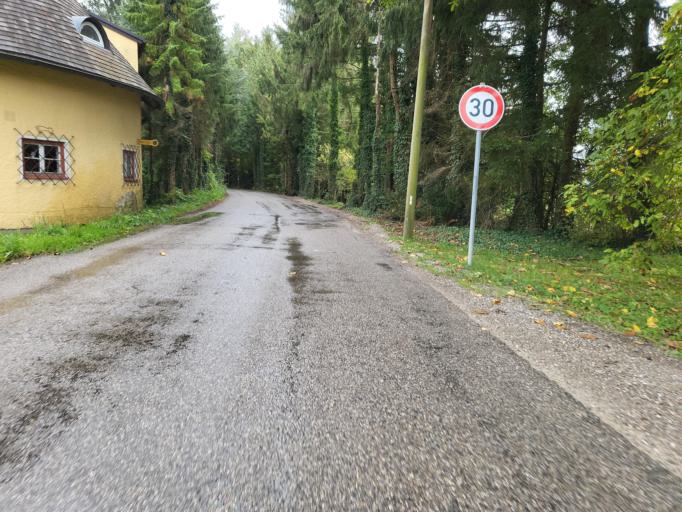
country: DE
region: Bavaria
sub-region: Upper Bavaria
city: Alling
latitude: 48.1568
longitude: 11.2795
